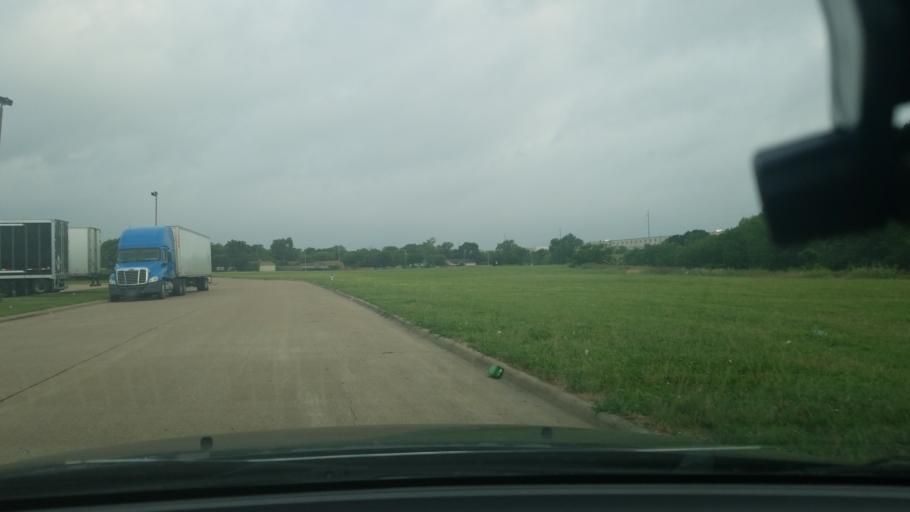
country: US
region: Texas
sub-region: Dallas County
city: Mesquite
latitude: 32.7709
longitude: -96.6259
